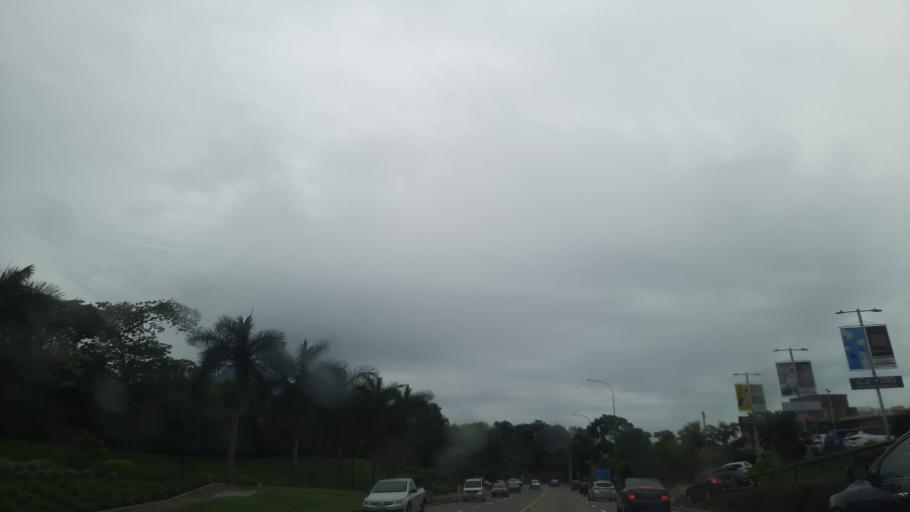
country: SV
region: La Libertad
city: Antiguo Cuscatlan
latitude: 13.6849
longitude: -89.2463
